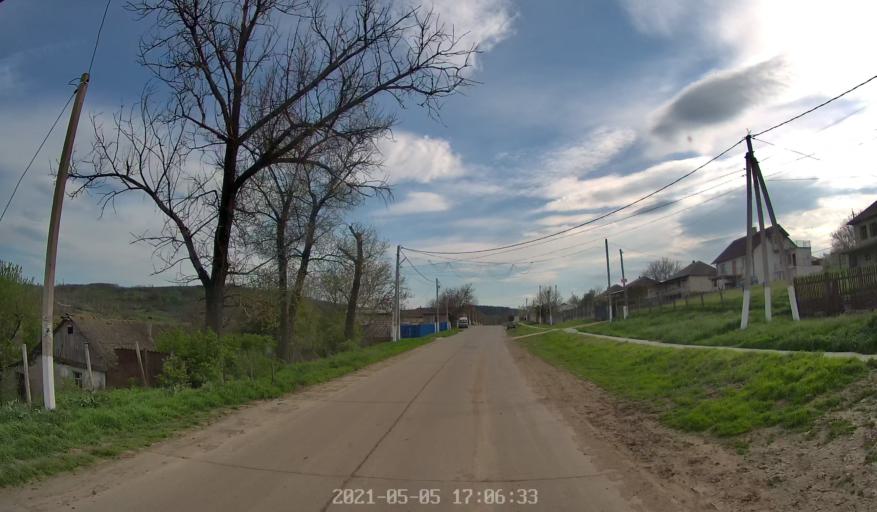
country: MD
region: Chisinau
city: Vadul lui Voda
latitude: 47.0193
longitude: 29.1391
